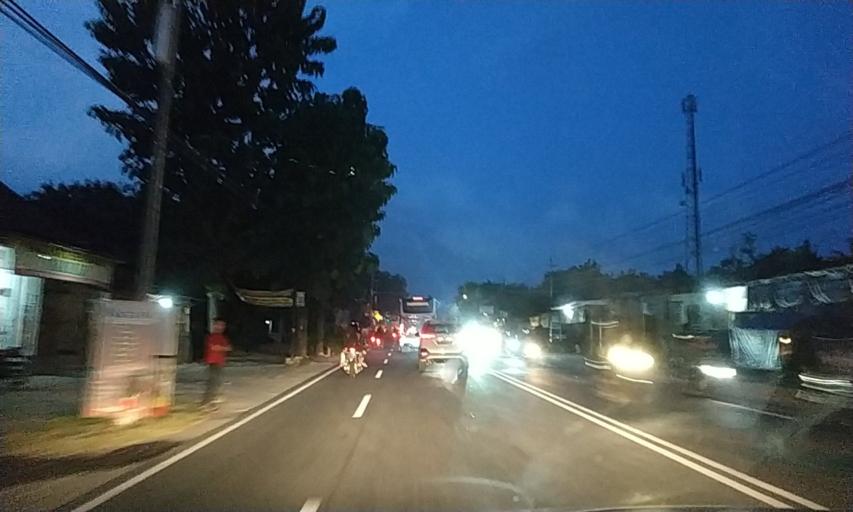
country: ID
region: Daerah Istimewa Yogyakarta
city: Godean
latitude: -7.8081
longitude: 110.2891
